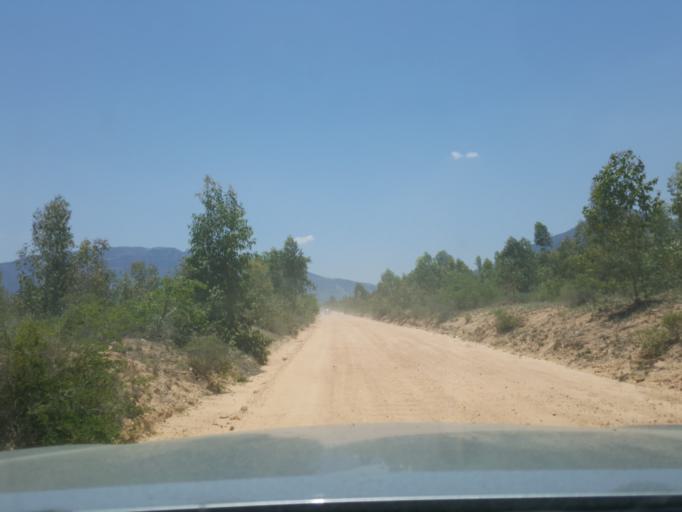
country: ZA
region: Limpopo
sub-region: Mopani District Municipality
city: Hoedspruit
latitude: -24.5866
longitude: 30.9707
